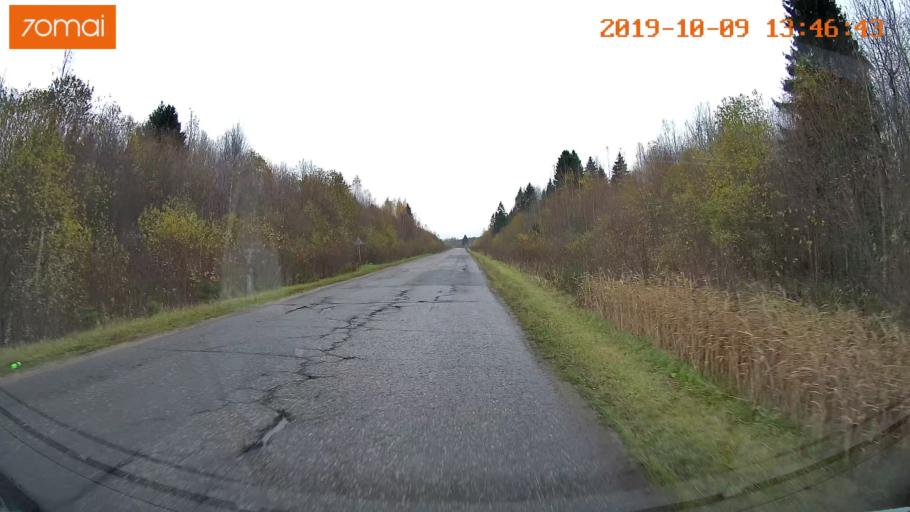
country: RU
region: Kostroma
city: Buy
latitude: 58.3856
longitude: 41.2196
